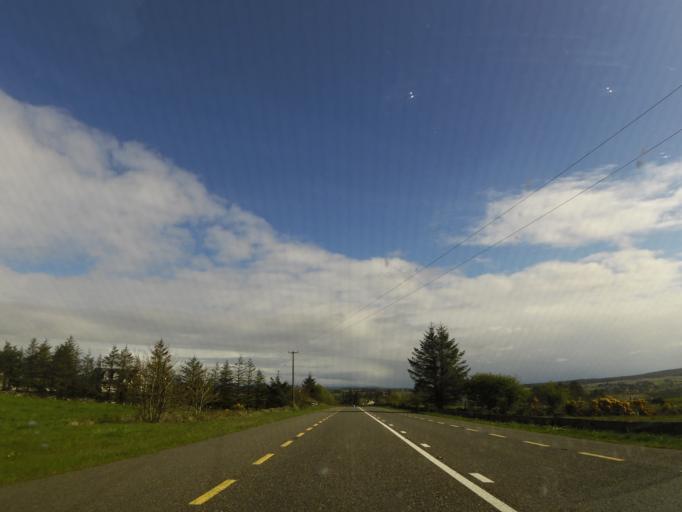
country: IE
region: Connaught
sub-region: Sligo
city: Tobercurry
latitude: 53.9192
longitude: -8.7877
